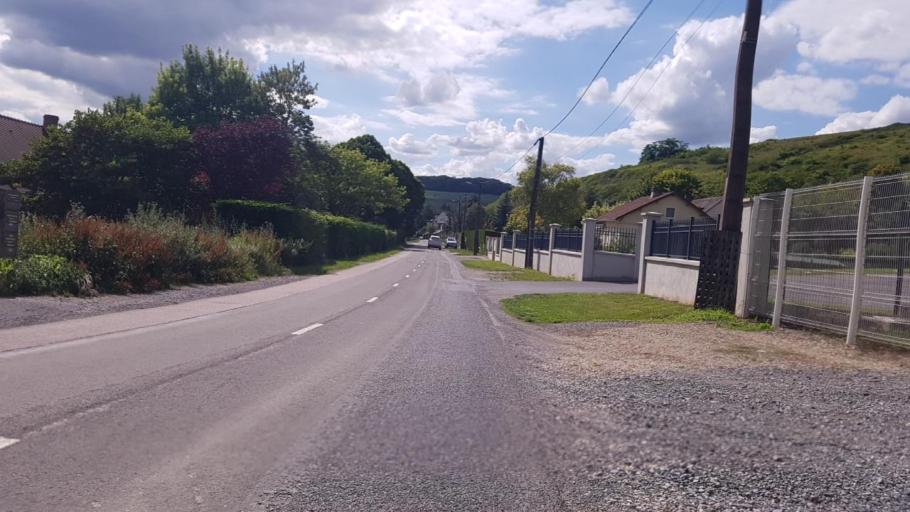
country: FR
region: Picardie
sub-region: Departement de l'Aisne
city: Crezancy
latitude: 49.0876
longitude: 3.5492
